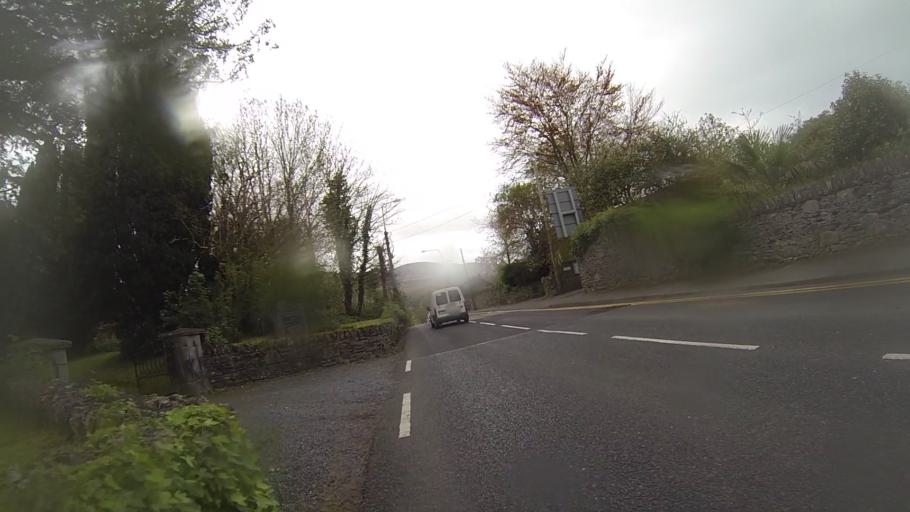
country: IE
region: Munster
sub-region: Ciarrai
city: Kenmare
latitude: 51.8773
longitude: -9.5836
